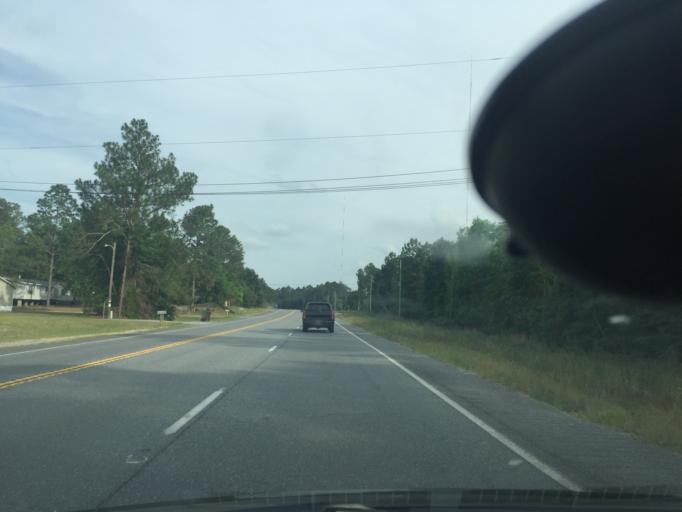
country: US
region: Georgia
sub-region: Chatham County
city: Bloomingdale
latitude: 32.0627
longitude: -81.3546
